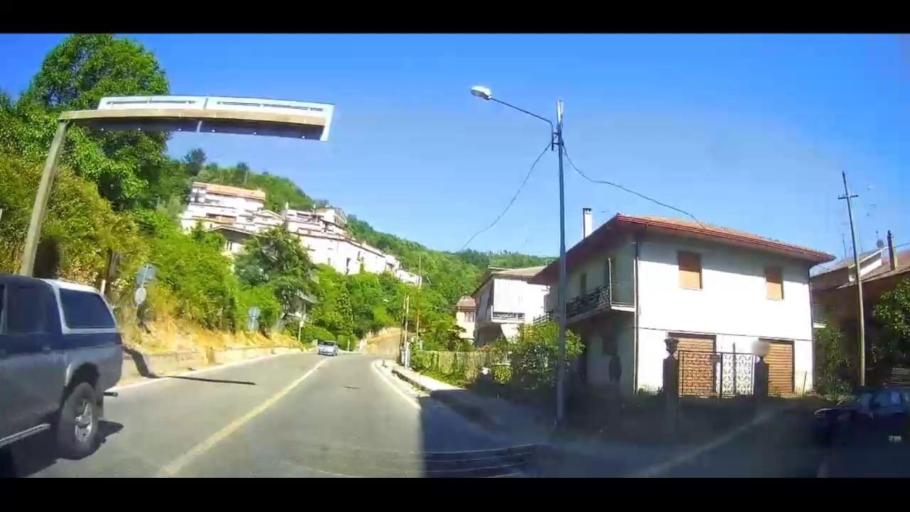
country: IT
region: Calabria
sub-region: Provincia di Cosenza
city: Celico
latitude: 39.3114
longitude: 16.3391
